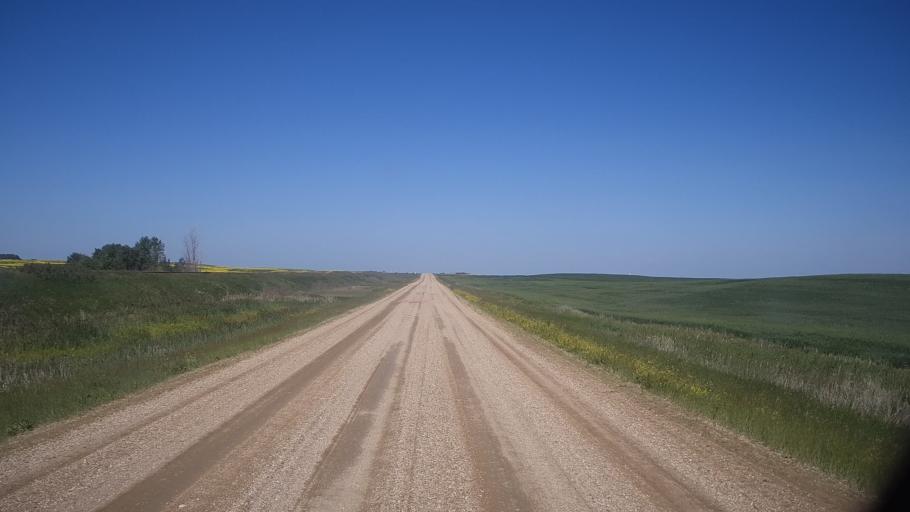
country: CA
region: Saskatchewan
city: Watrous
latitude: 51.8498
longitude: -105.9321
